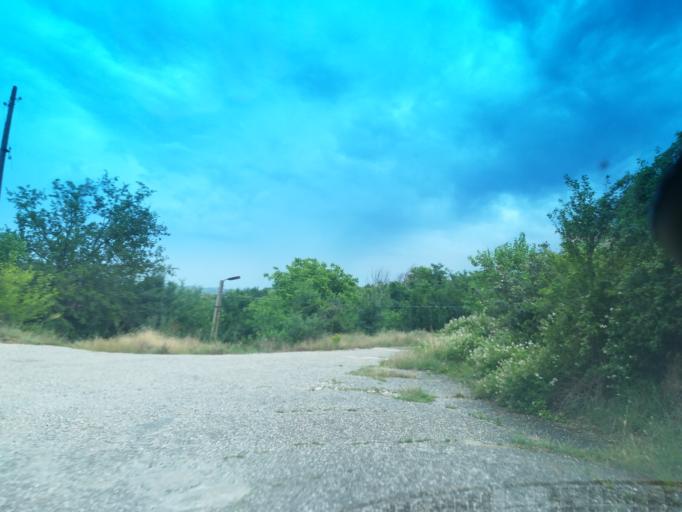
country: BG
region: Khaskovo
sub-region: Obshtina Mineralni Bani
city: Mineralni Bani
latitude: 41.9919
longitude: 25.2325
